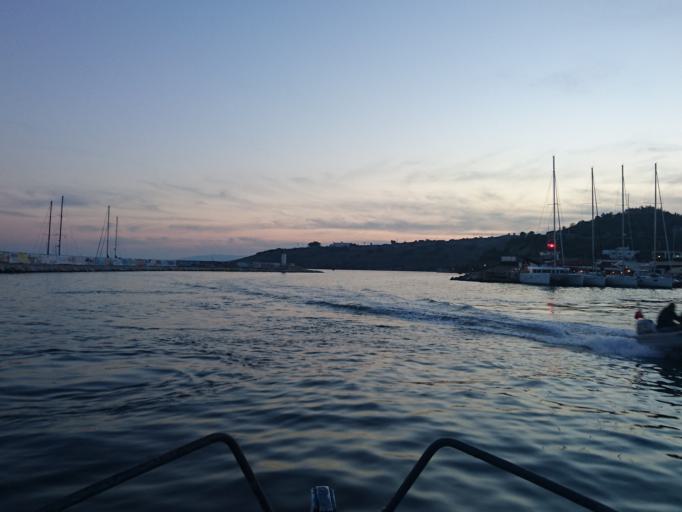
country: TR
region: Mugla
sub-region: Bodrum
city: Bodrum
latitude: 37.0329
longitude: 27.4261
